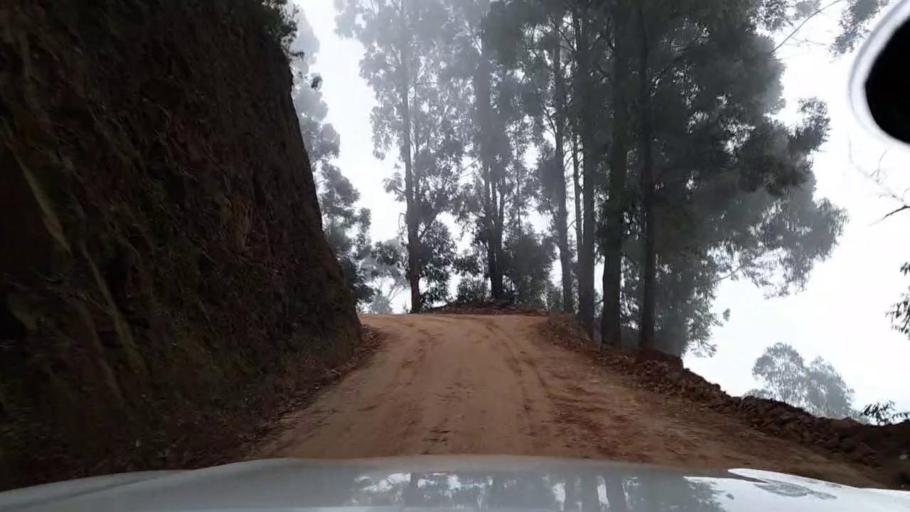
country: RW
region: Western Province
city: Cyangugu
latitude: -2.5875
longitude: 29.1877
